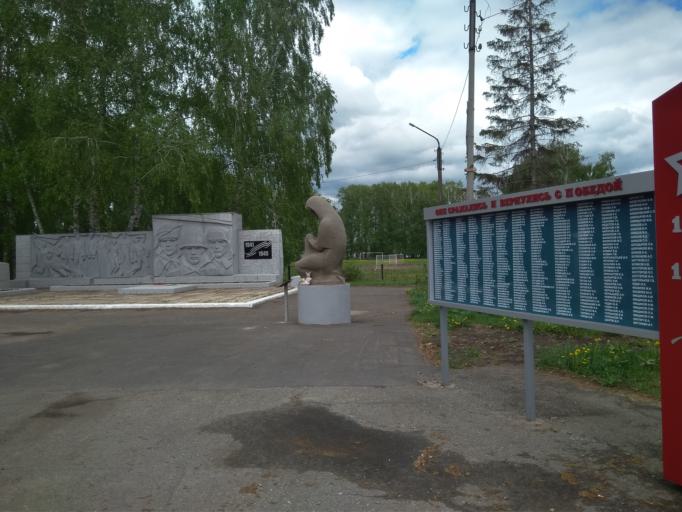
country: RU
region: Ulyanovsk
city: Staraya Mayna
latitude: 54.6056
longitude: 48.9294
